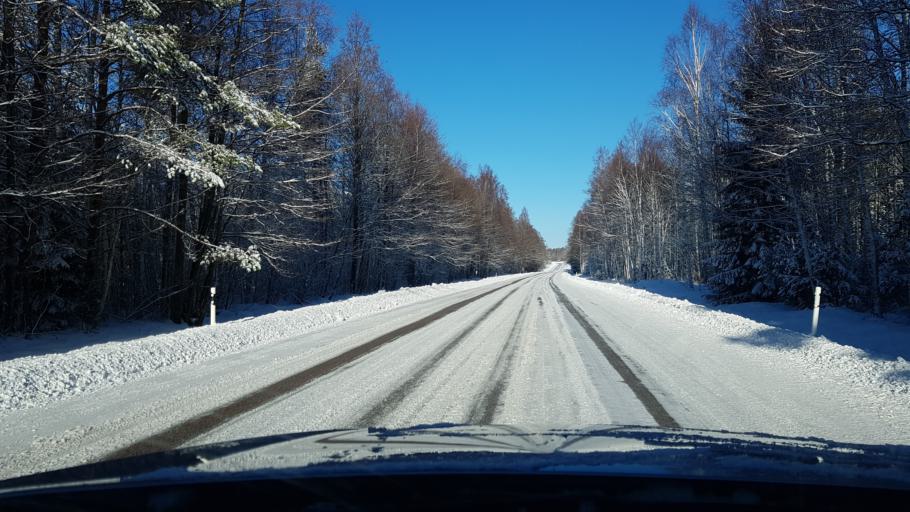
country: EE
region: Hiiumaa
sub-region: Kaerdla linn
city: Kardla
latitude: 58.9114
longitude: 22.7924
